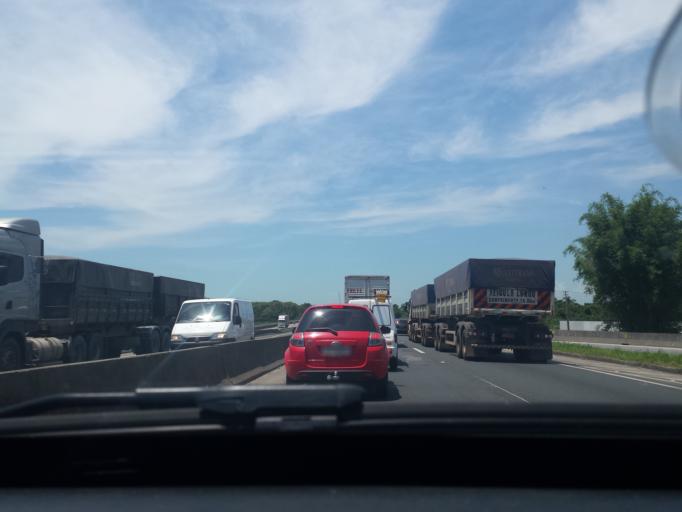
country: BR
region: Santa Catarina
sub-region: Itapema
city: Itapema
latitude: -27.1335
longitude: -48.6099
